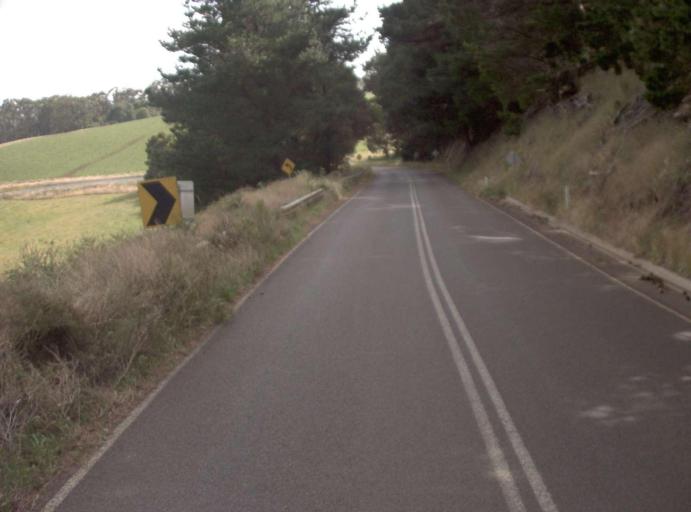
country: AU
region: Victoria
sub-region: Latrobe
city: Moe
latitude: -38.2420
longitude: 146.1676
